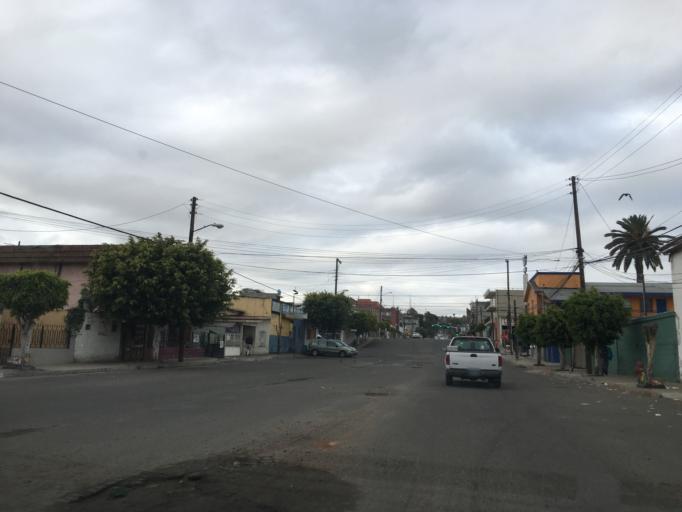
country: MX
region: Baja California
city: Tijuana
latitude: 32.5366
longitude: -117.0475
